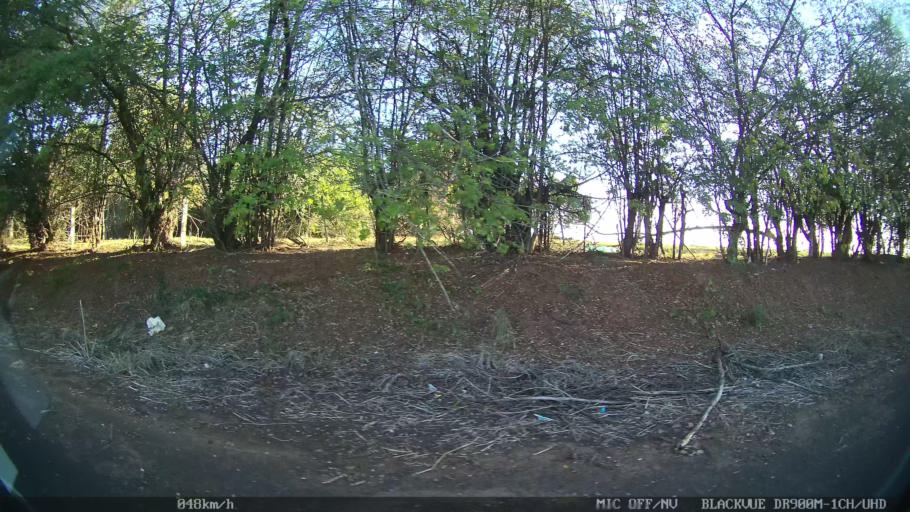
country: BR
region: Sao Paulo
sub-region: Sao Jose Do Rio Preto
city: Sao Jose do Rio Preto
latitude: -20.8679
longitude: -49.3291
